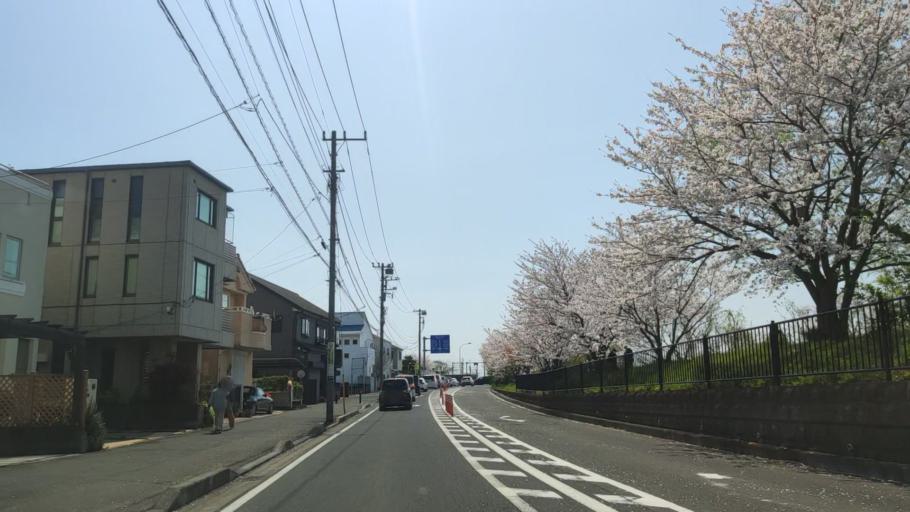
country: JP
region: Kanagawa
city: Hiratsuka
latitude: 35.3250
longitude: 139.3286
